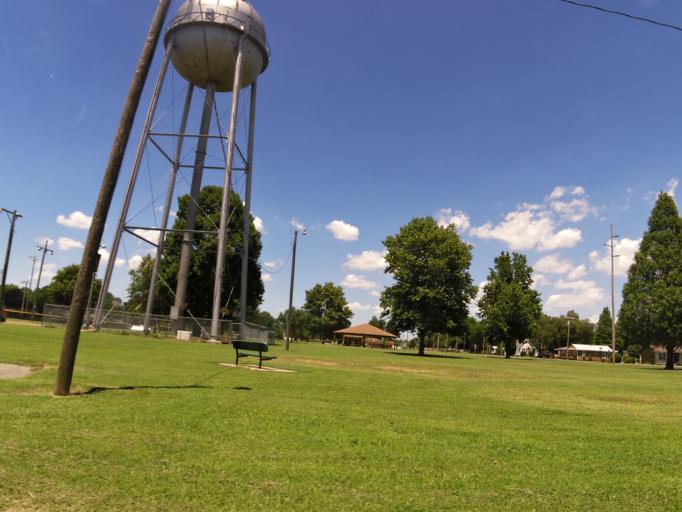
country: US
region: Missouri
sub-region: New Madrid County
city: New Madrid
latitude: 36.5861
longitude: -89.5369
